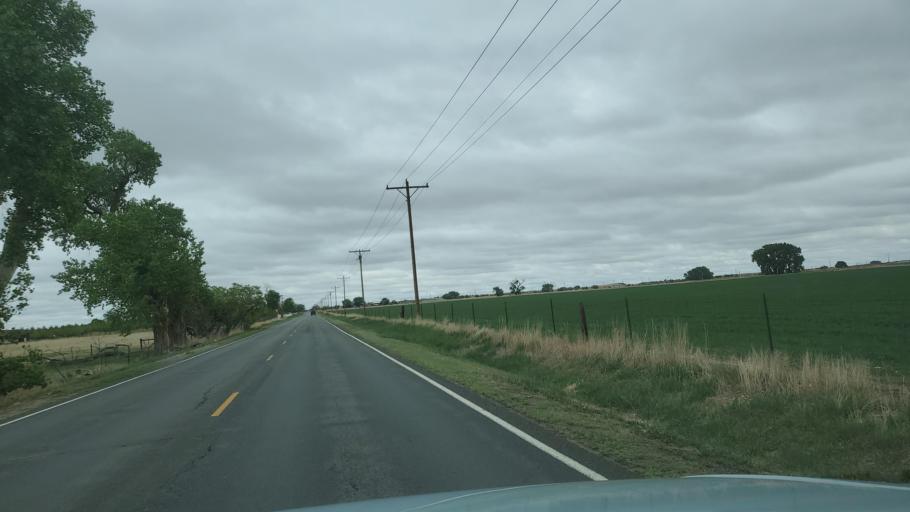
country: US
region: Colorado
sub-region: Weld County
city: Lochbuie
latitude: 39.9724
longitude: -104.7221
